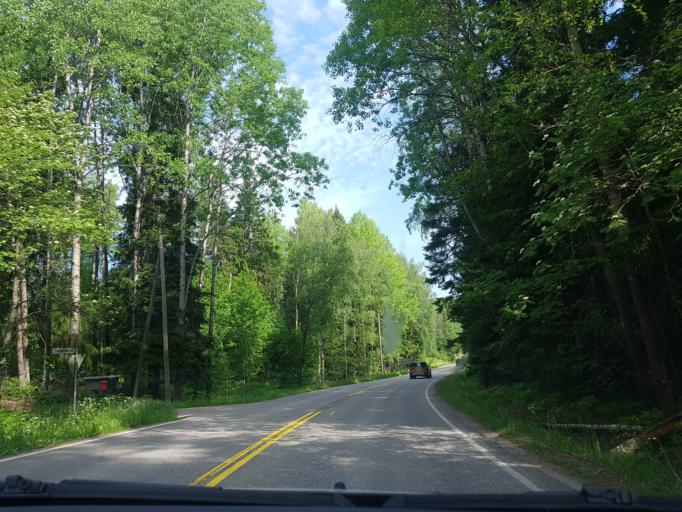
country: FI
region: Uusimaa
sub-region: Helsinki
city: Vihti
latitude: 60.2956
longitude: 24.3976
